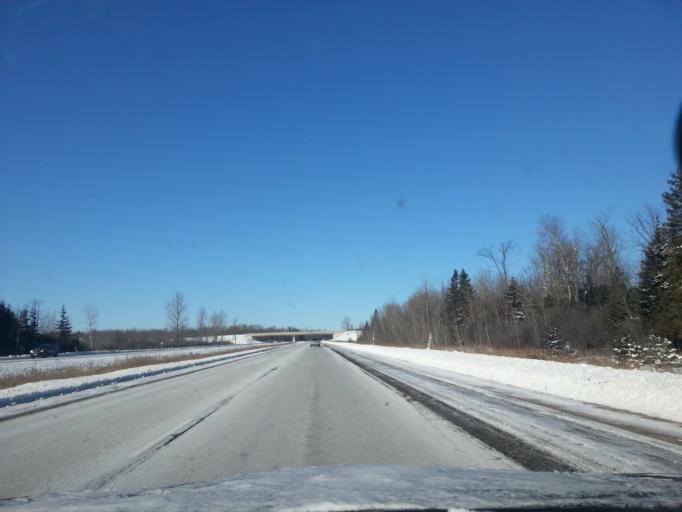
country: CA
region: Ontario
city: Bells Corners
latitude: 45.2950
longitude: -76.0190
